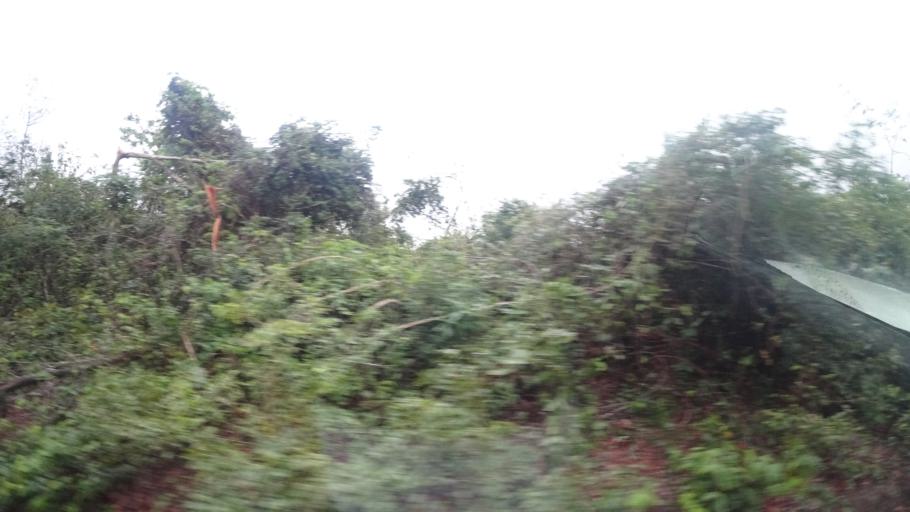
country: MZ
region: Sofala
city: Dondo
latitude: -19.5781
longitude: 35.1509
